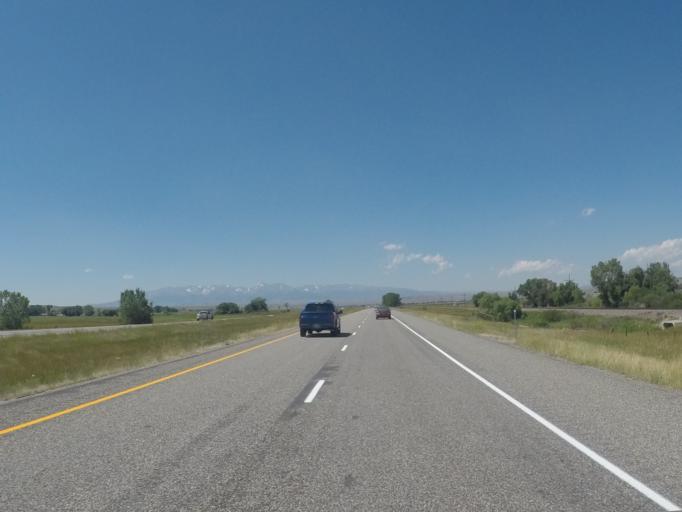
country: US
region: Montana
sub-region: Sweet Grass County
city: Big Timber
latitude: 45.8019
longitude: -109.8502
